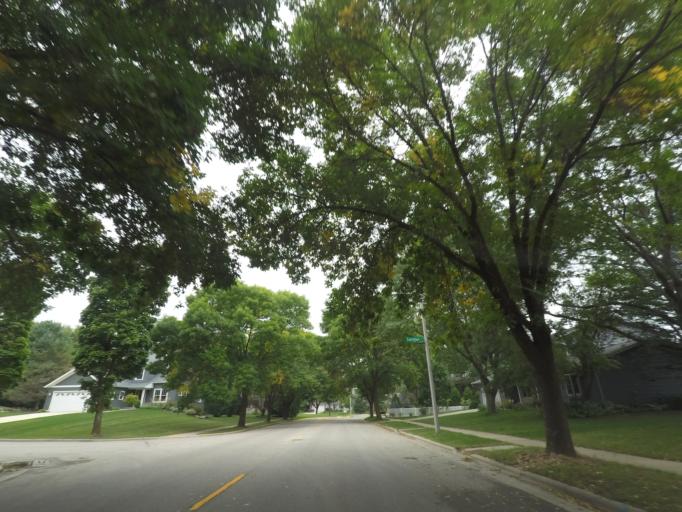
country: US
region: Wisconsin
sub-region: Dane County
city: Middleton
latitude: 43.0852
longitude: -89.5123
